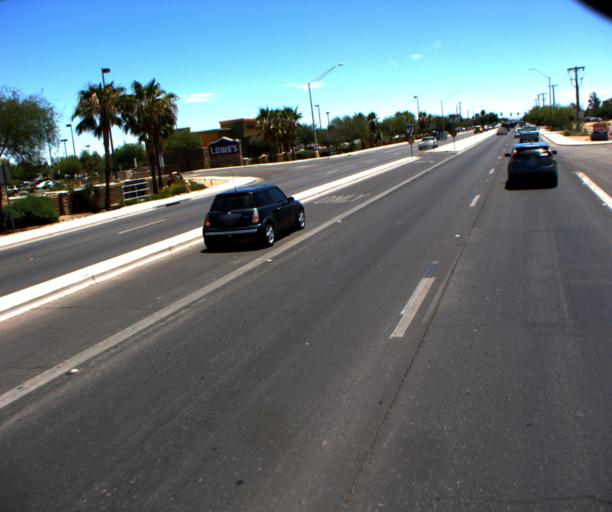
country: US
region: Arizona
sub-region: Pinal County
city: Casa Grande
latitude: 32.8795
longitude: -111.7262
